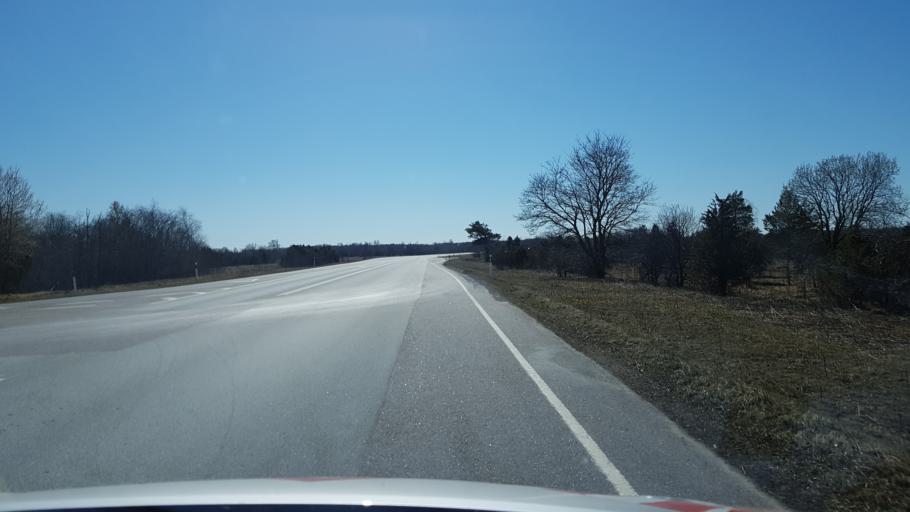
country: EE
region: Laeaene-Virumaa
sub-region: Viru-Nigula vald
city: Kunda
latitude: 59.4705
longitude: 26.4804
